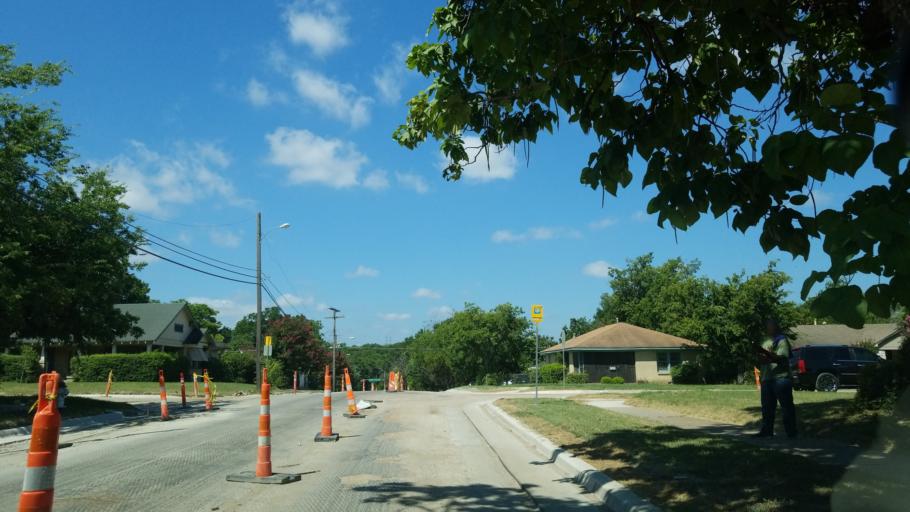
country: US
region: Texas
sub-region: Dallas County
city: Dallas
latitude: 32.7297
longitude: -96.7973
